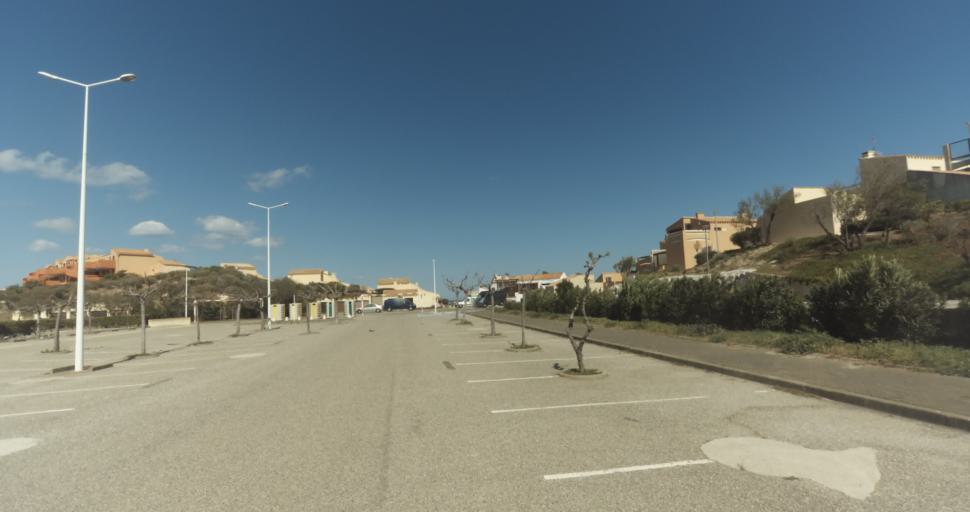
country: FR
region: Languedoc-Roussillon
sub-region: Departement de l'Aude
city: Leucate
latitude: 42.8525
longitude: 3.0428
